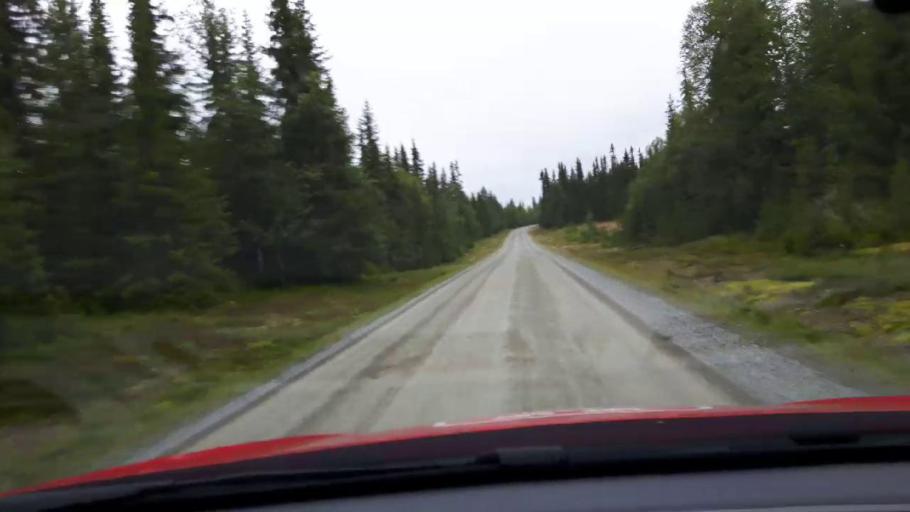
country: SE
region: Jaemtland
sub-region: Bergs Kommun
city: Hoverberg
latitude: 62.8615
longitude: 13.9460
